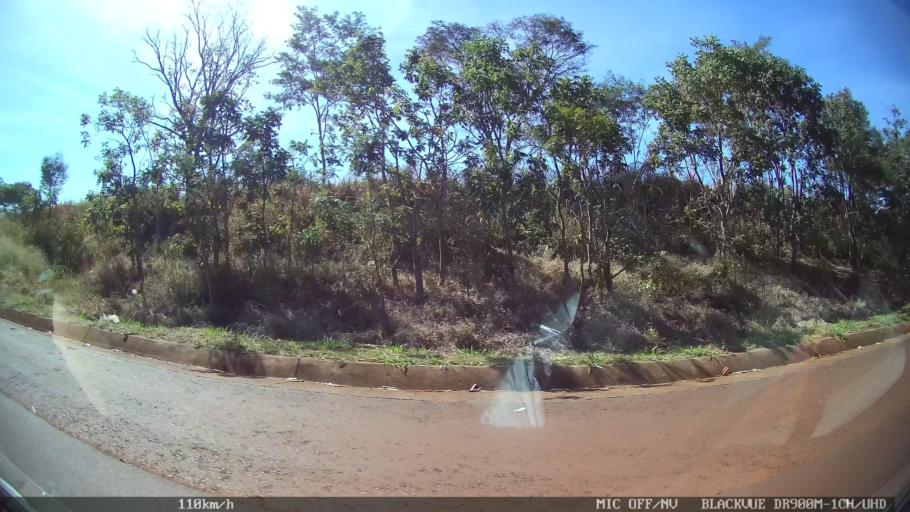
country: BR
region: Sao Paulo
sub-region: Sao Joaquim Da Barra
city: Sao Joaquim da Barra
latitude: -20.5359
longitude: -47.8264
